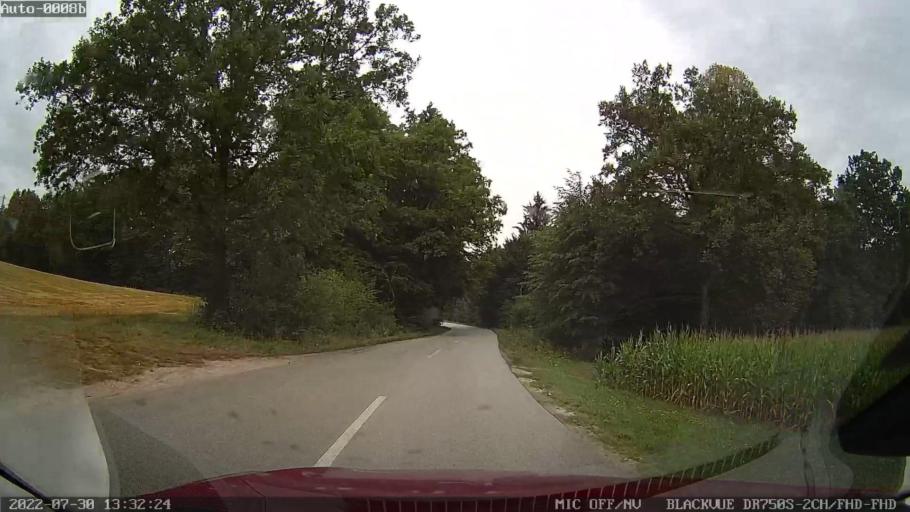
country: SI
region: Zuzemberk
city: Zuzemberk
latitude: 45.8415
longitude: 14.9391
